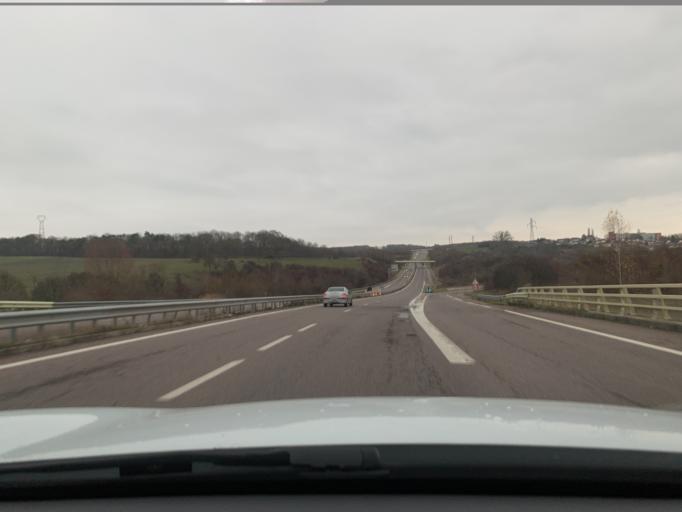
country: FR
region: Lorraine
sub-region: Departement de la Moselle
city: Sarreguemines
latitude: 49.1091
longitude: 7.0285
